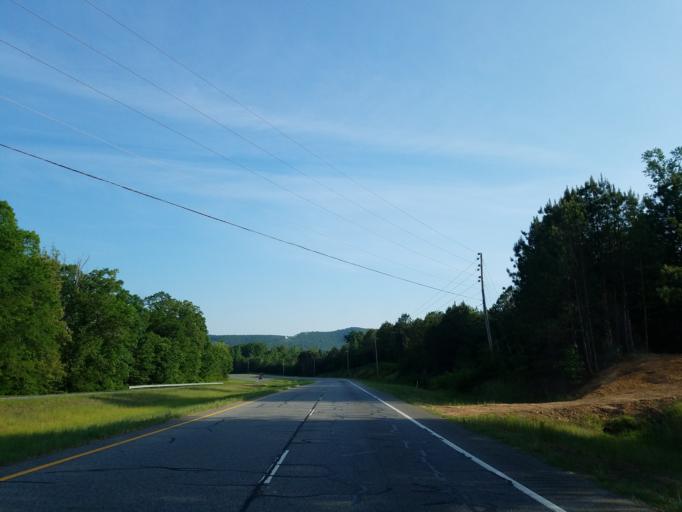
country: US
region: Georgia
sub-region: Chattooga County
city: Summerville
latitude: 34.4304
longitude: -85.2494
